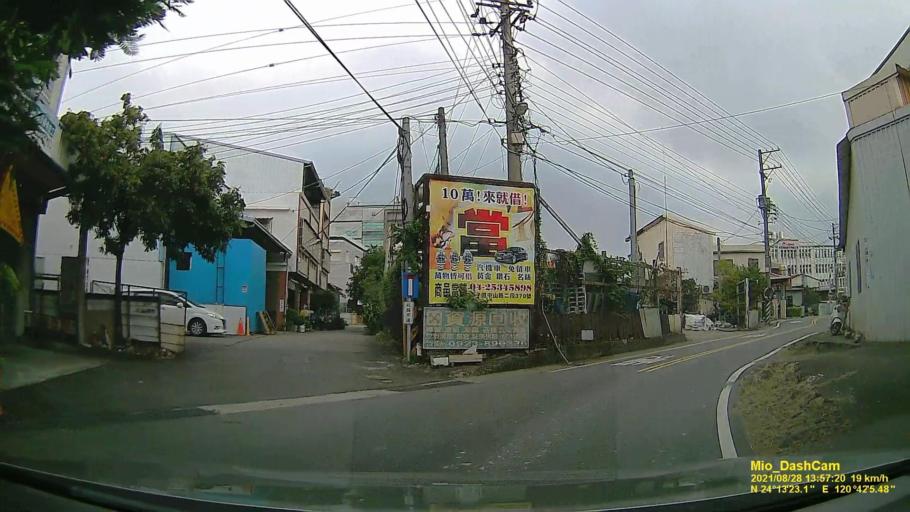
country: TW
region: Taiwan
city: Fengyuan
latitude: 24.2231
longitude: 120.7015
